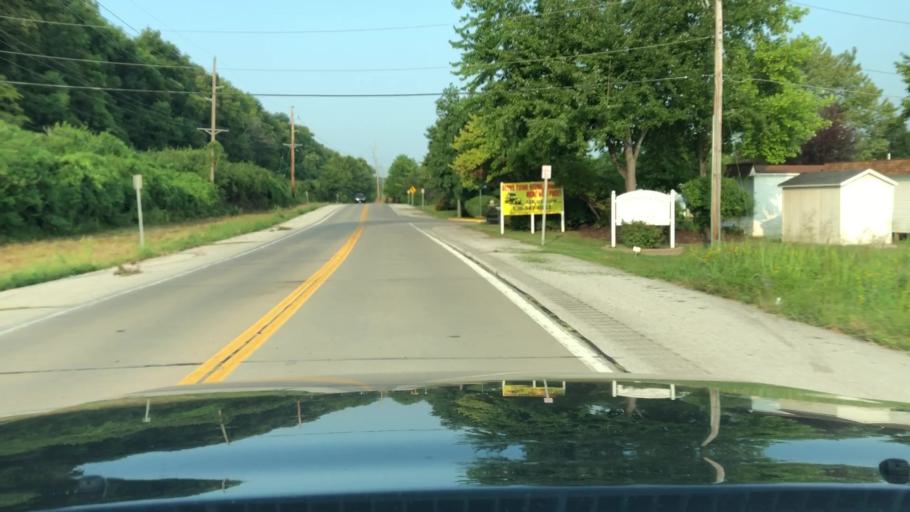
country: US
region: Missouri
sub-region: Saint Charles County
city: Saint Charles
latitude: 38.8161
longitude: -90.5201
